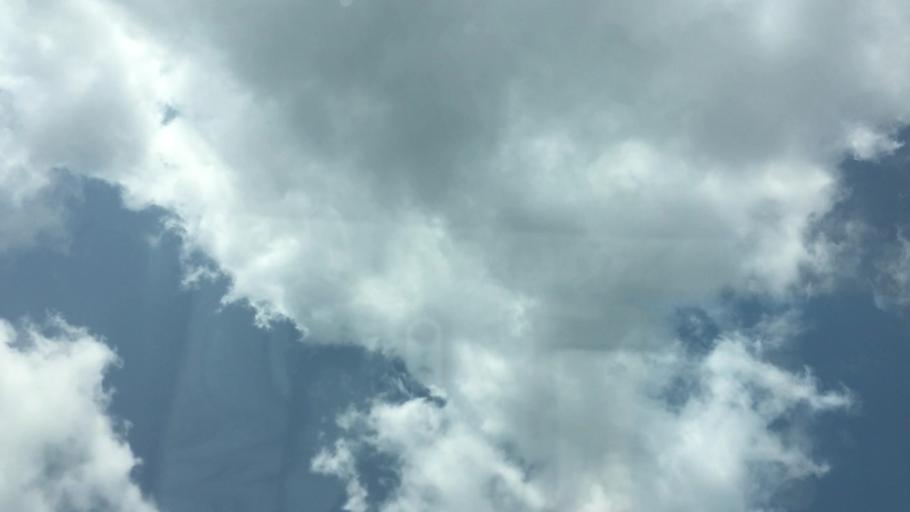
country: US
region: Alabama
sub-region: Pickens County
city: Gordo
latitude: 33.2735
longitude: -87.7548
